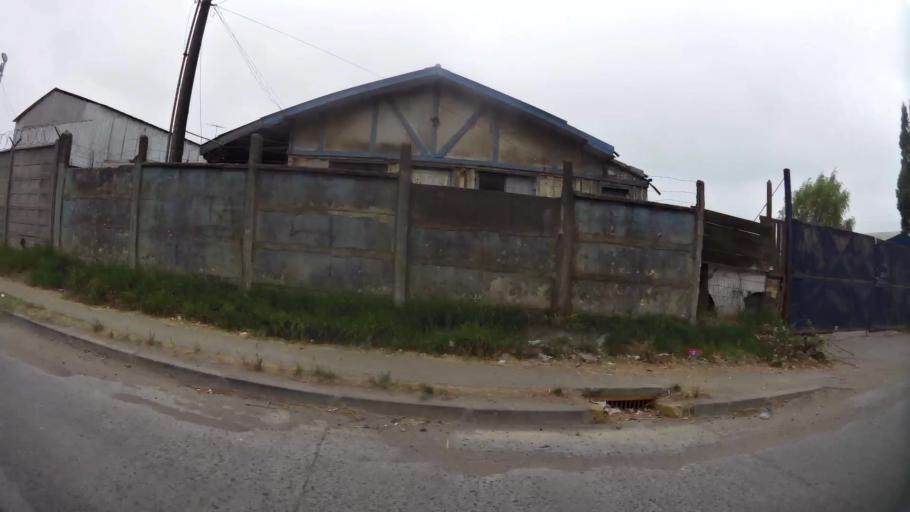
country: CL
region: Biobio
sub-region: Provincia de Concepcion
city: Concepcion
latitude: -36.8214
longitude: -72.9919
